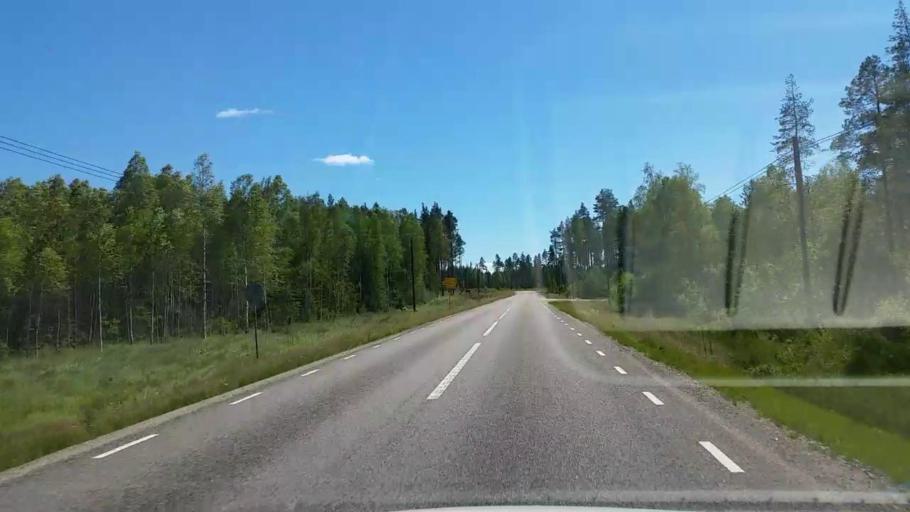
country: SE
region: Gaevleborg
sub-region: Ovanakers Kommun
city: Edsbyn
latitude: 61.4611
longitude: 15.7000
